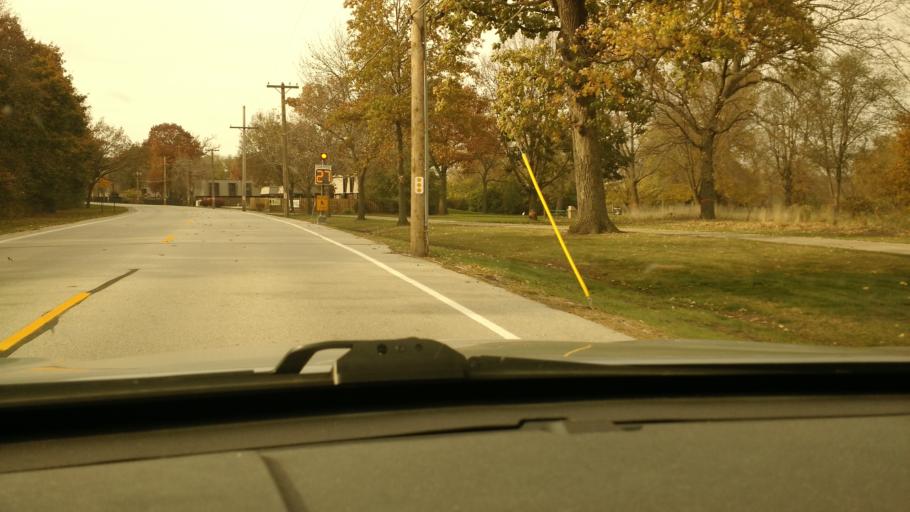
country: US
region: Iowa
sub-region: Scott County
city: Bettendorf
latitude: 41.5175
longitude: -90.5290
